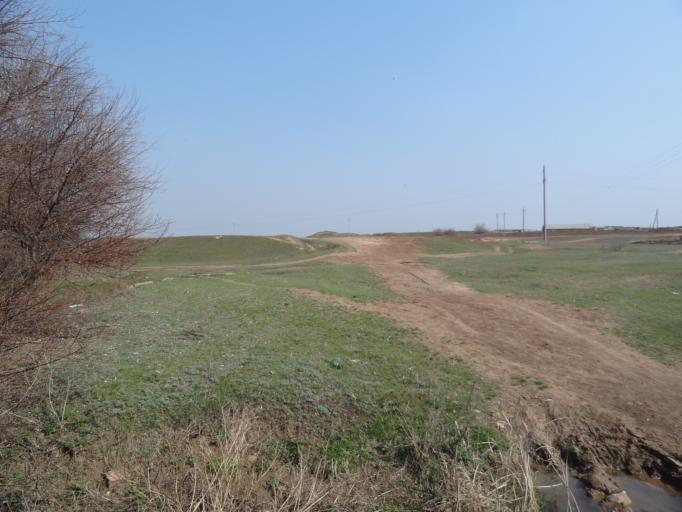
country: RU
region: Saratov
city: Privolzhskiy
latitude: 51.3070
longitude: 45.9646
